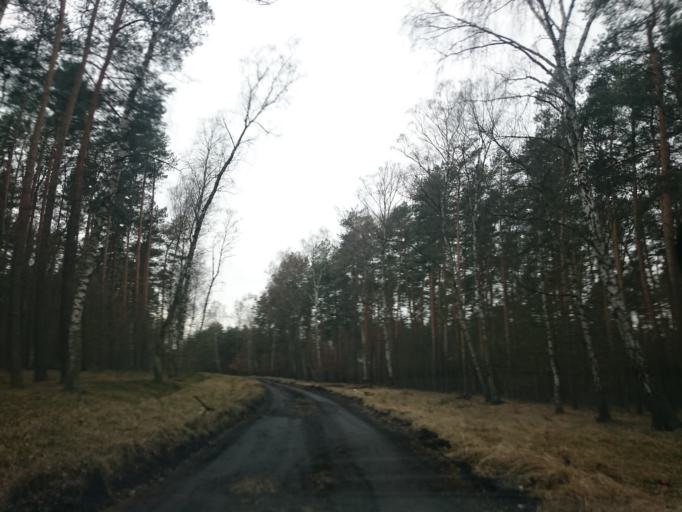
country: PL
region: Kujawsko-Pomorskie
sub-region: Powiat golubsko-dobrzynski
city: Ciechocin
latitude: 53.0748
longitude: 18.9070
